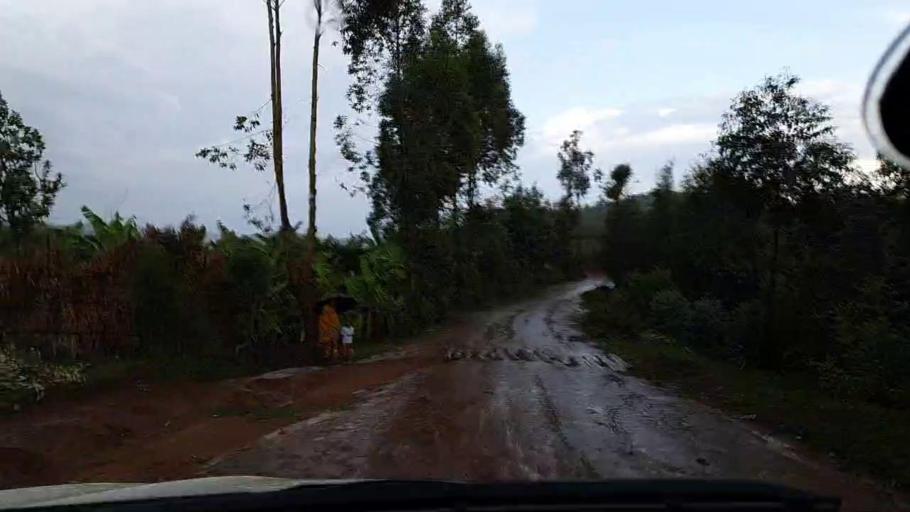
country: BI
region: Kayanza
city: Kayanza
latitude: -2.7730
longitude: 29.5446
